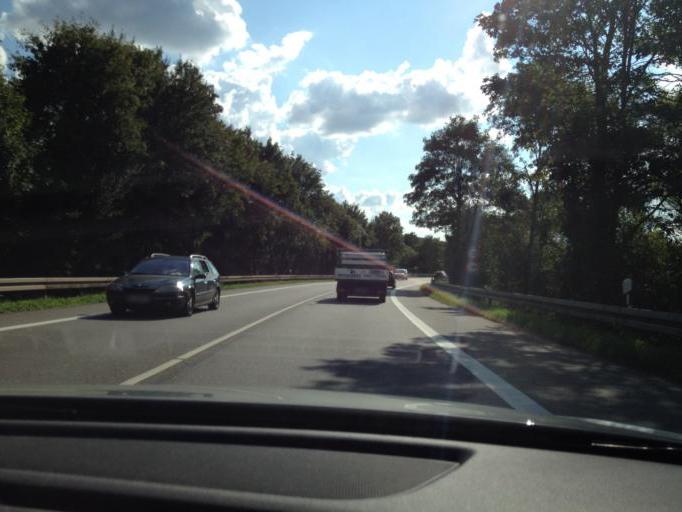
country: DE
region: Saarland
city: Lebach
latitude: 49.4108
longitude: 6.9158
